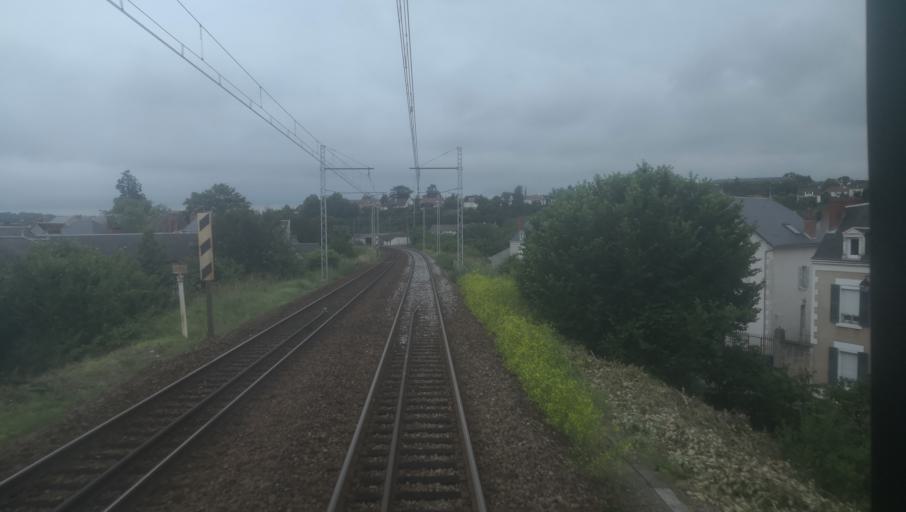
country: FR
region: Centre
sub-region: Departement de l'Indre
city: Argenton-sur-Creuse
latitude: 46.5847
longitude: 1.5246
